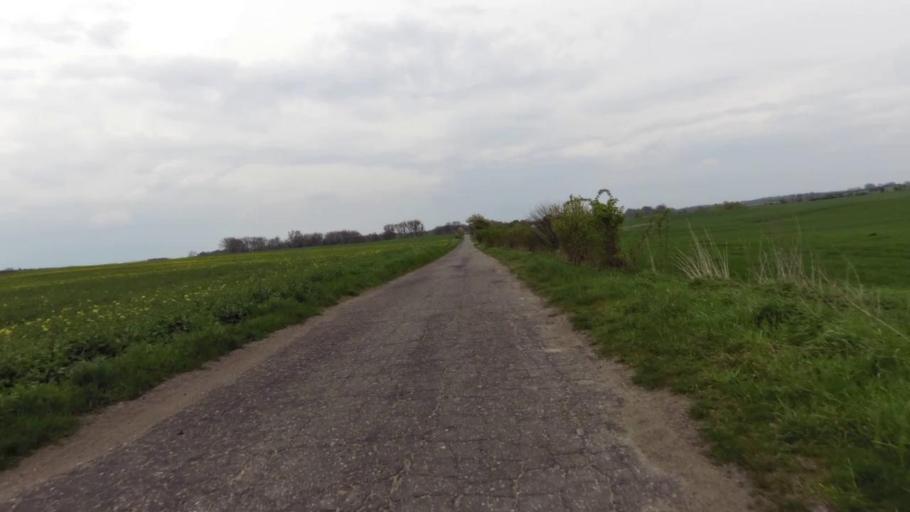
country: PL
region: West Pomeranian Voivodeship
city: Trzcinsko Zdroj
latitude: 52.9473
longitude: 14.7082
